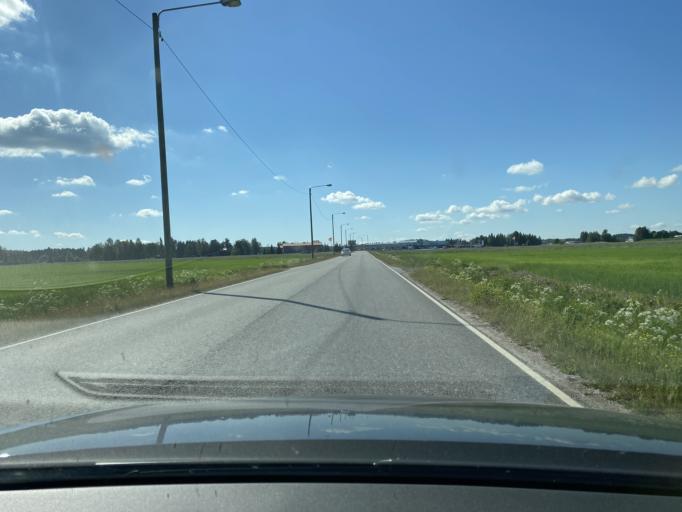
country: FI
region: Satakunta
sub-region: Pori
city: Huittinen
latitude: 61.1649
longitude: 22.7005
